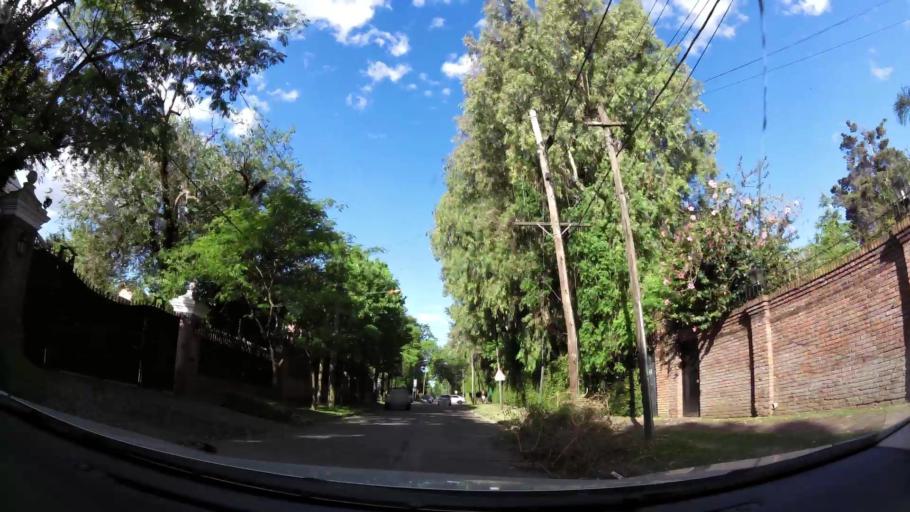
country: AR
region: Buenos Aires
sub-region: Partido de San Isidro
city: San Isidro
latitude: -34.4834
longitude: -58.5525
